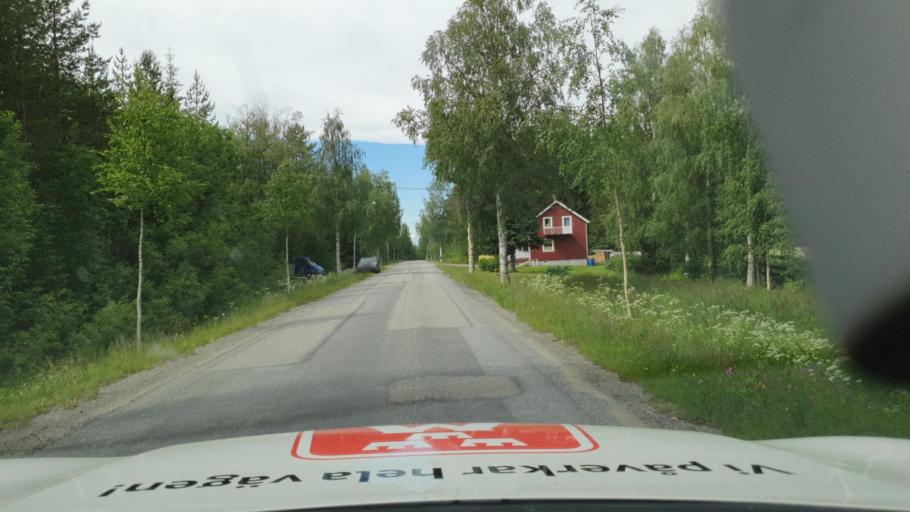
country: SE
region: Vaesterbotten
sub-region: Skelleftea Kommun
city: Burtraesk
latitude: 64.4402
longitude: 20.4936
